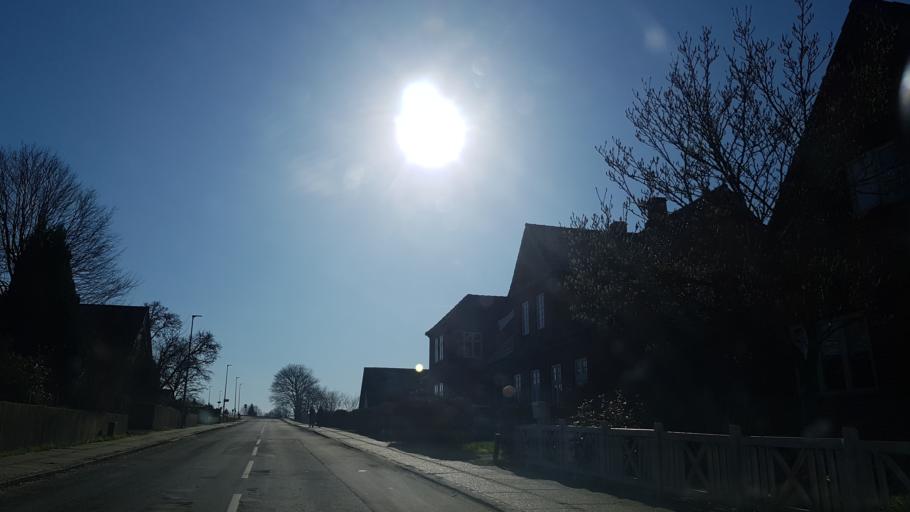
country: DK
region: South Denmark
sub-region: Kolding Kommune
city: Lunderskov
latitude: 55.4773
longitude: 9.3020
